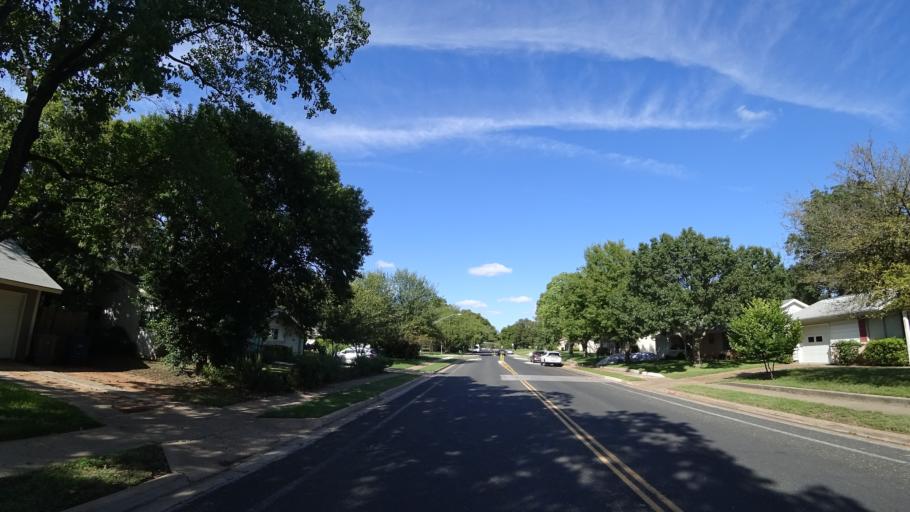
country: US
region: Texas
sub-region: Williamson County
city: Jollyville
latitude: 30.3621
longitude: -97.7368
